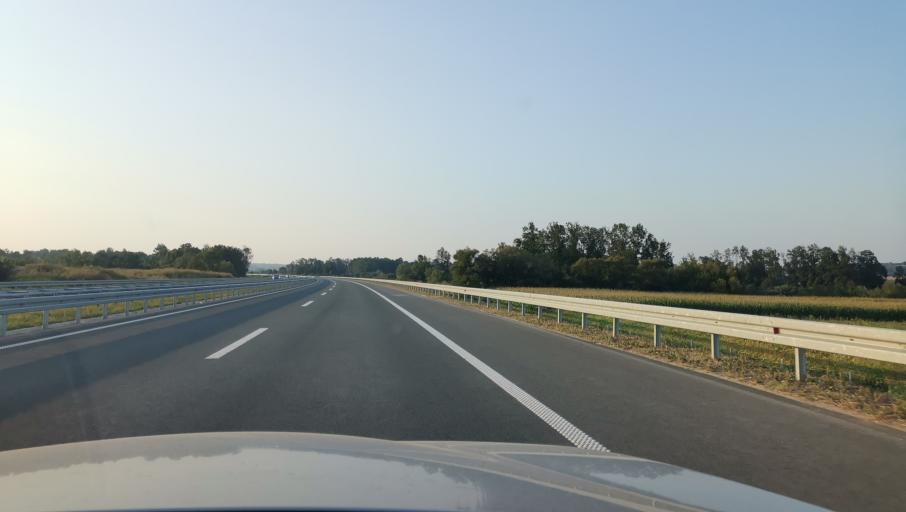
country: RS
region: Central Serbia
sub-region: Kolubarski Okrug
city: Ljig
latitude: 44.2637
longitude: 20.2708
